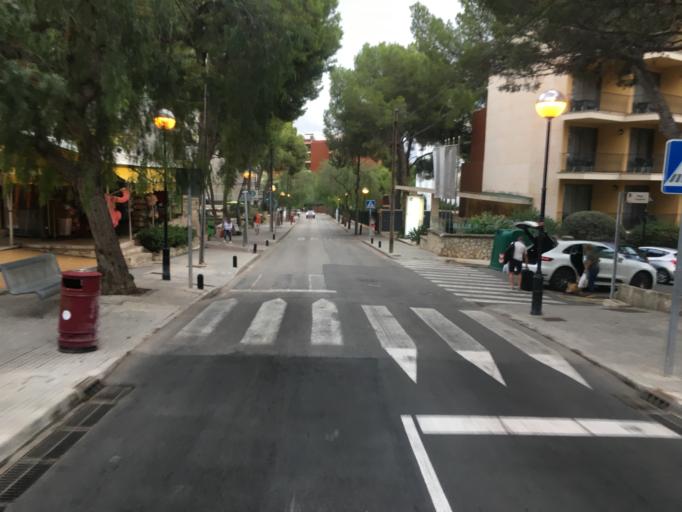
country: ES
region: Balearic Islands
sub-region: Illes Balears
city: Palma
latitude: 39.5426
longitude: 2.5944
